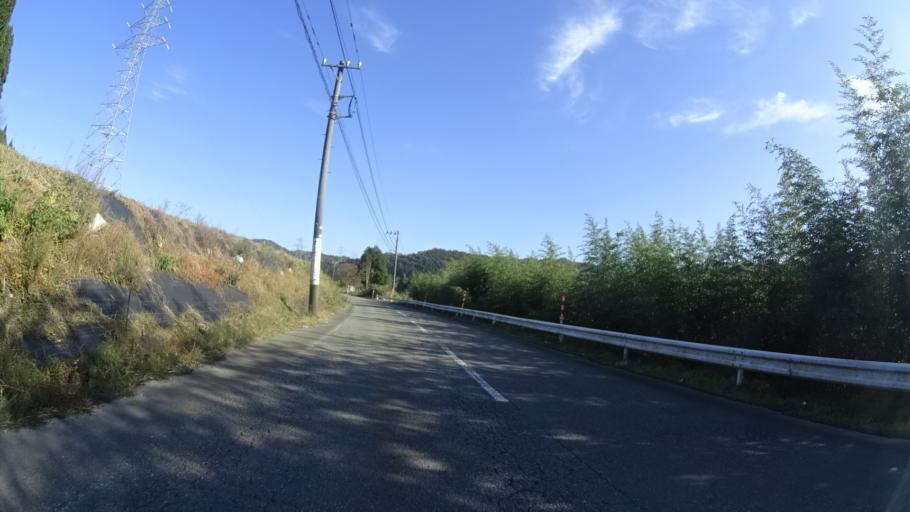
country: JP
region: Ishikawa
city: Komatsu
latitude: 36.2627
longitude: 136.3928
